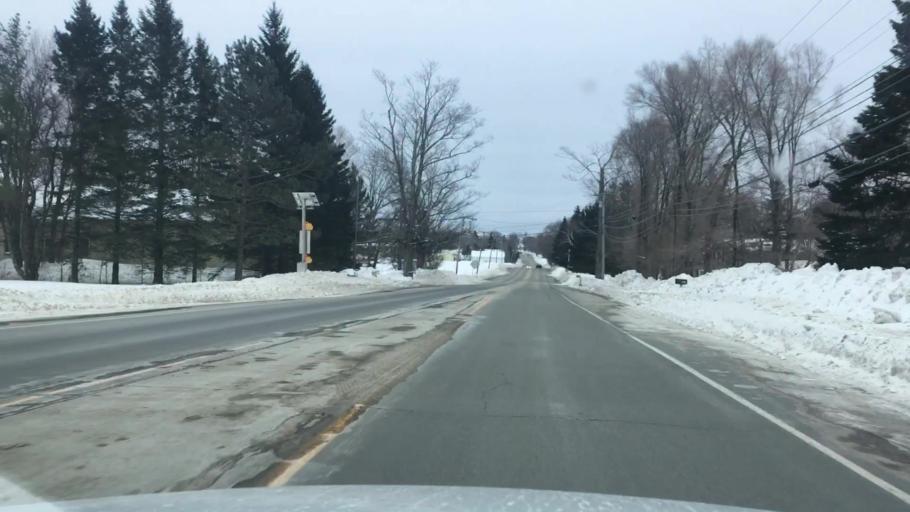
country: US
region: Maine
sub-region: Penobscot County
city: Charleston
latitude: 45.0160
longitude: -69.0277
